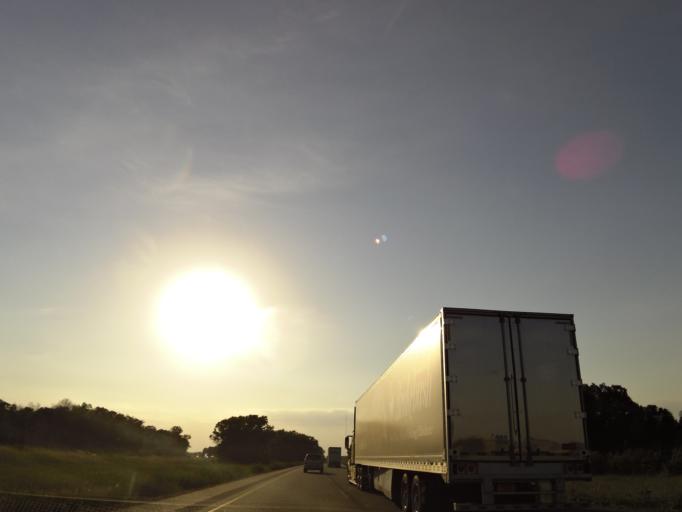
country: US
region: Wisconsin
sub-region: Monroe County
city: Tomah
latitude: 43.9812
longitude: -90.4284
